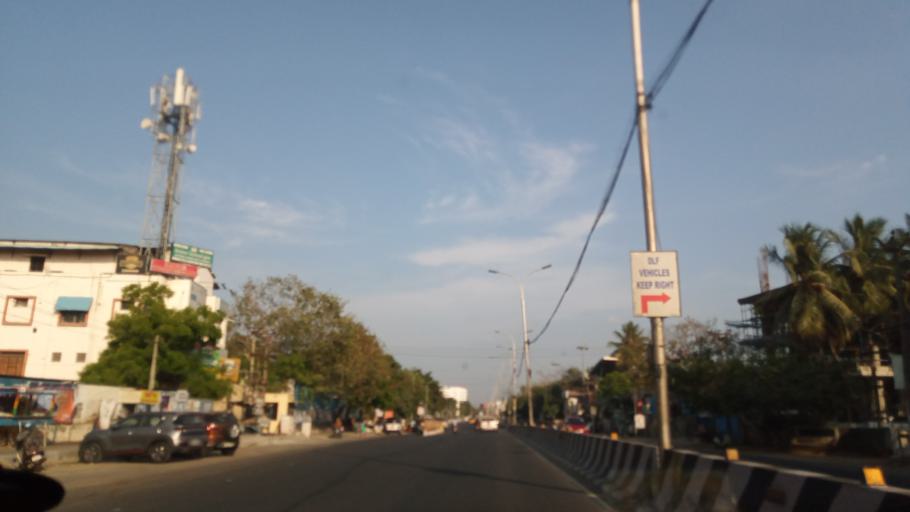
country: IN
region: Tamil Nadu
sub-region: Kancheepuram
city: Manappakkam
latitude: 13.0253
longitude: 80.1761
